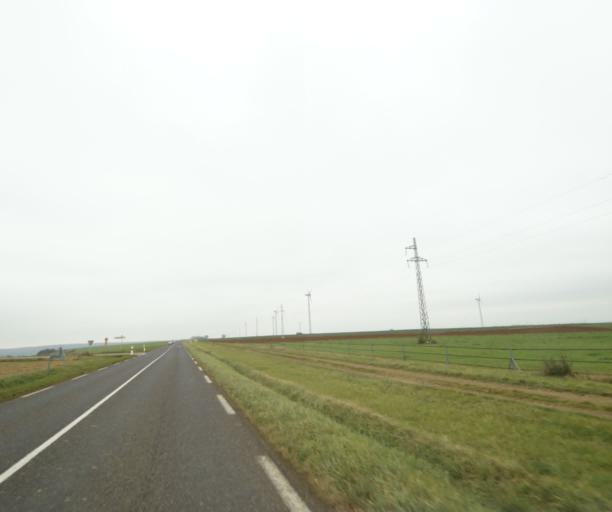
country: FR
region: Lorraine
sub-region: Departement de Meurthe-et-Moselle
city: Mancieulles
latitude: 49.2769
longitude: 5.8778
